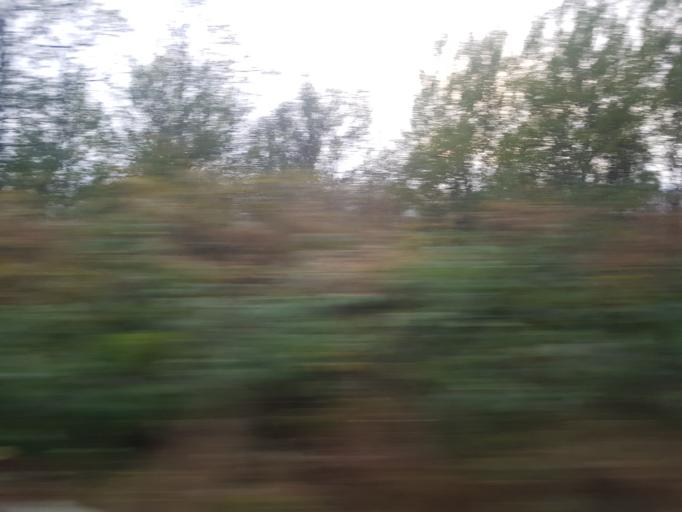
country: NO
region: Oppland
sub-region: Dovre
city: Dombas
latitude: 62.0438
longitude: 9.1505
